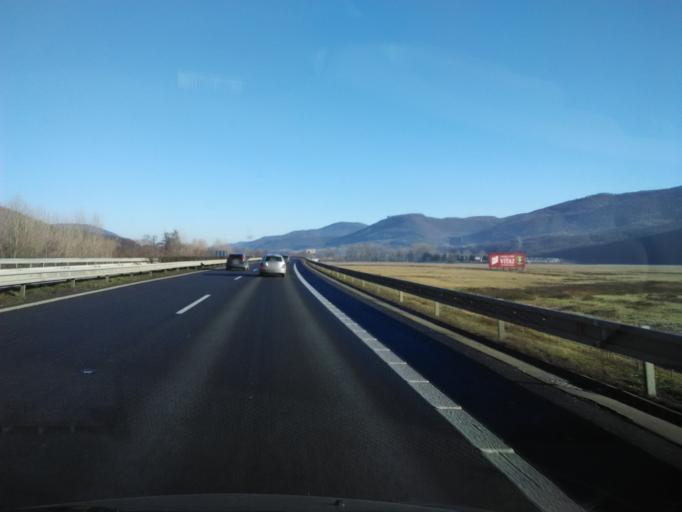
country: SK
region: Banskobystricky
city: Nova Bana
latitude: 48.3672
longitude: 18.5871
